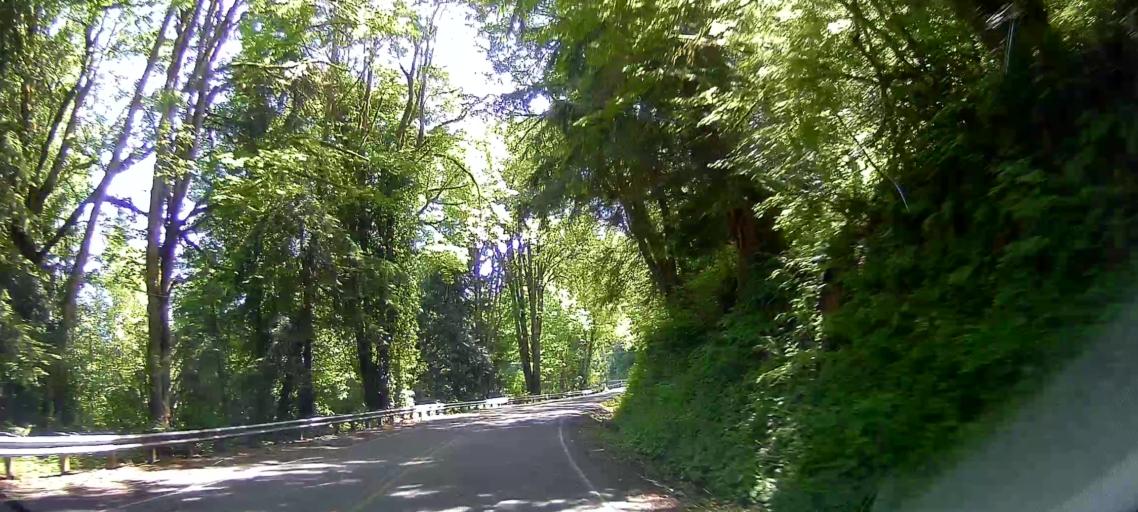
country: US
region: Washington
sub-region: Skagit County
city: Sedro-Woolley
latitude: 48.5516
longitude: -122.3002
